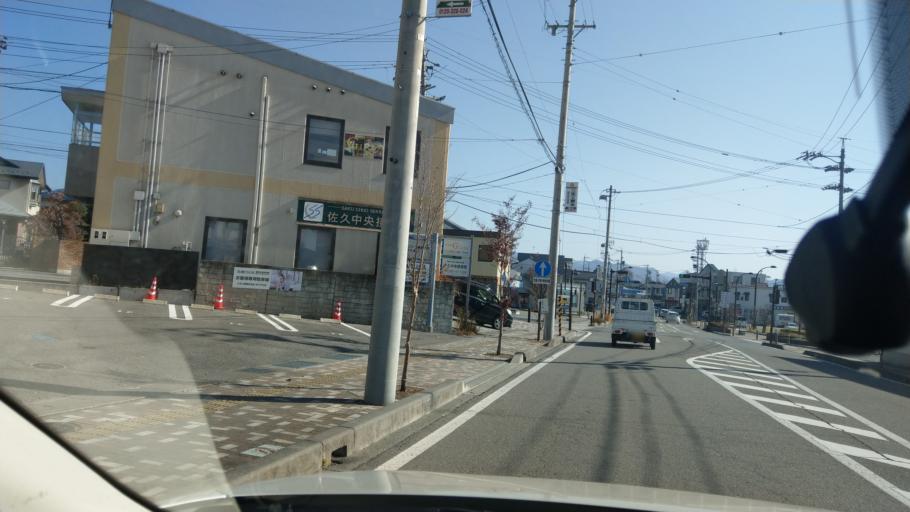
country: JP
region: Nagano
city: Komoro
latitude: 36.2754
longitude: 138.4717
